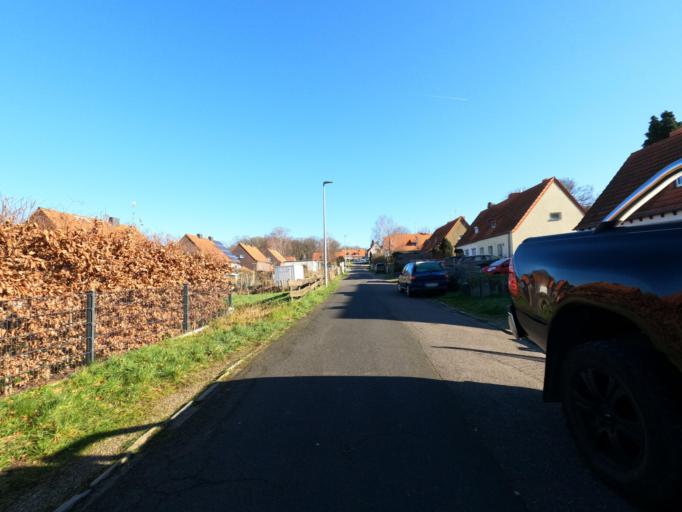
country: DE
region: North Rhine-Westphalia
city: Huckelhoven
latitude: 51.0615
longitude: 6.2260
